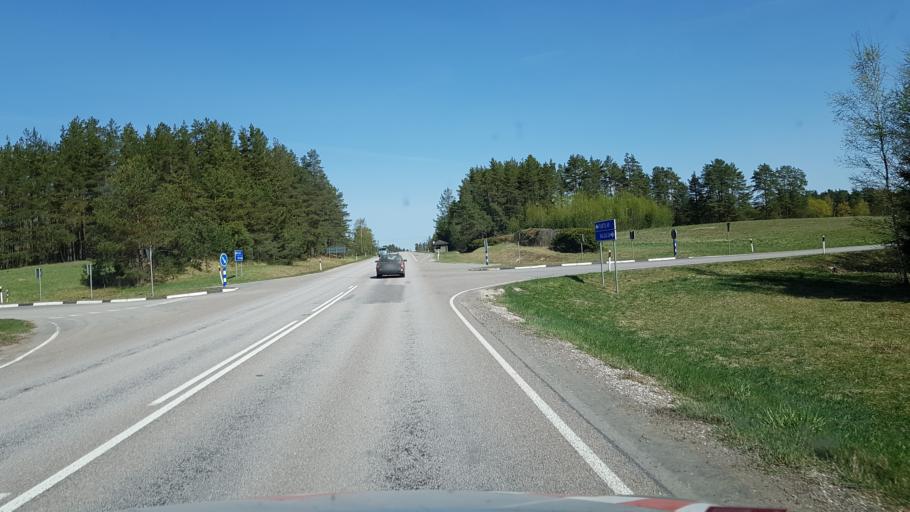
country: EE
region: Tartu
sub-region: Elva linn
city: Elva
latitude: 58.0726
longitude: 26.2048
